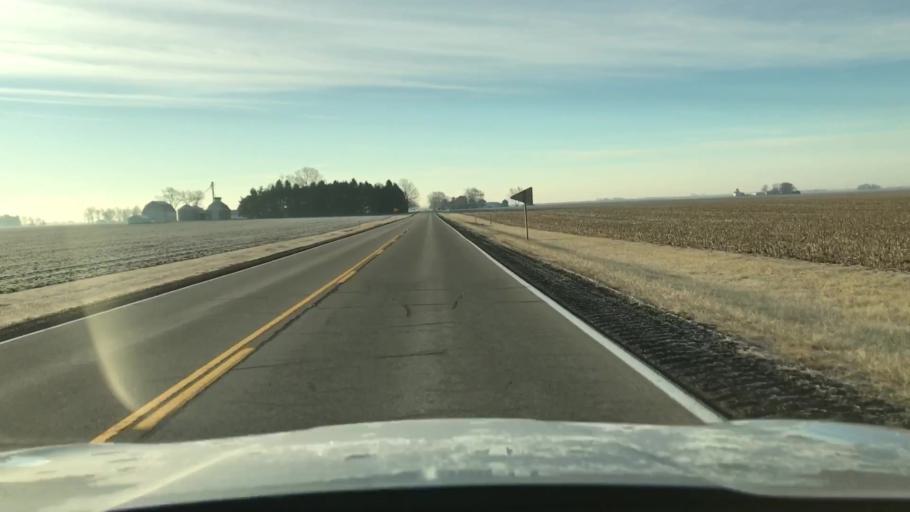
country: US
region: Illinois
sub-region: McLean County
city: Hudson
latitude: 40.6176
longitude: -88.9455
